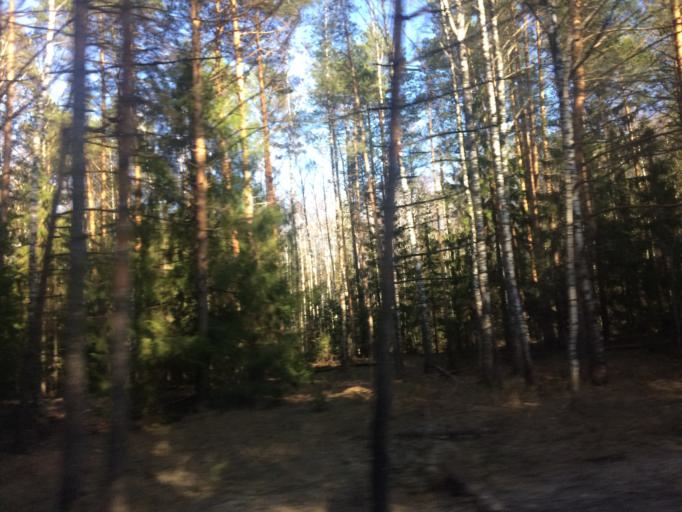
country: RU
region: Tatarstan
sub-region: Zelenodol'skiy Rayon
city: Vasil'yevo
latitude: 55.8945
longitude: 48.7287
